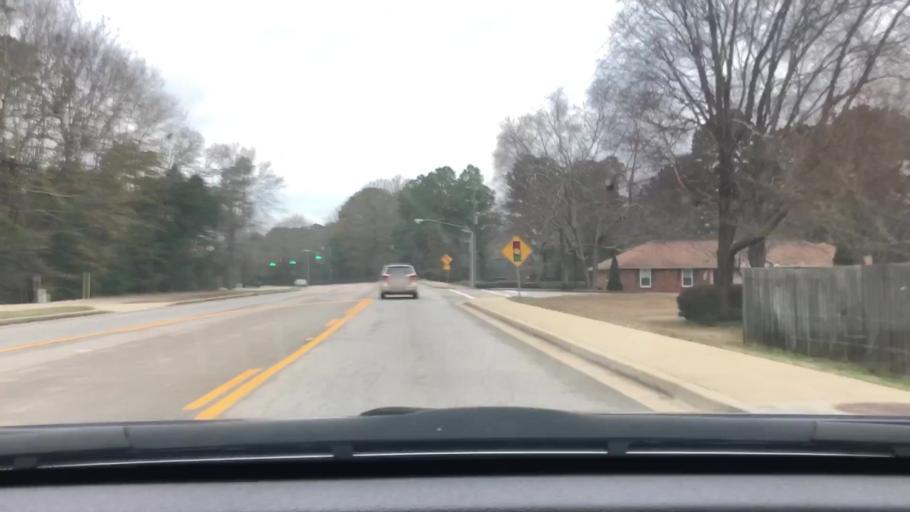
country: US
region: South Carolina
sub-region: Sumter County
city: Cane Savannah
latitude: 33.9244
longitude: -80.4018
